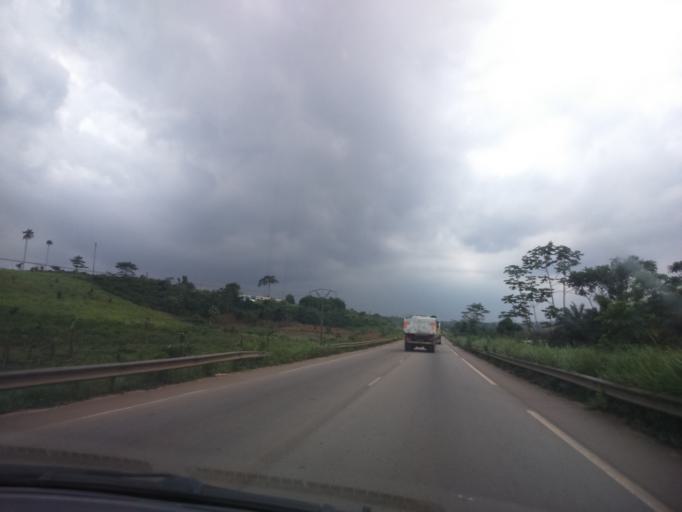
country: CI
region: Lagunes
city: Anyama
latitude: 5.5054
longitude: -4.0635
